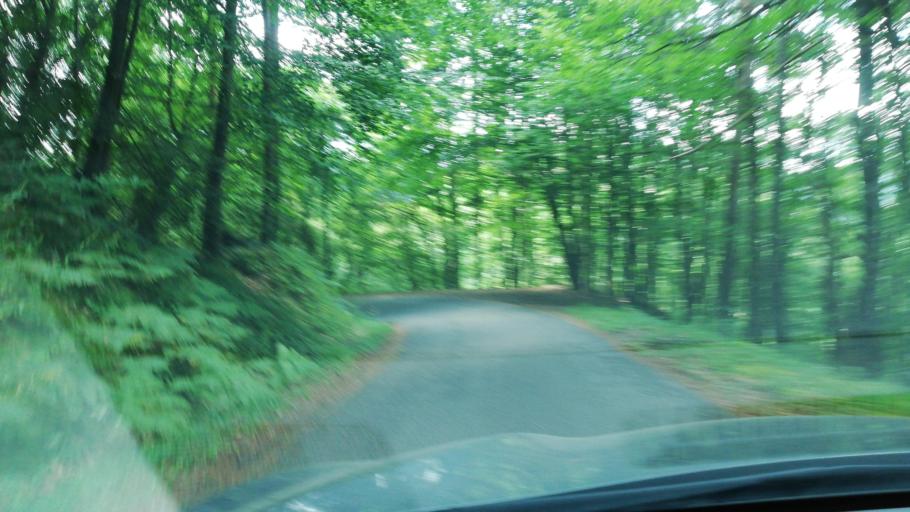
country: FR
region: Limousin
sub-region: Departement de la Correze
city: Argentat
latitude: 44.9787
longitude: 2.0336
